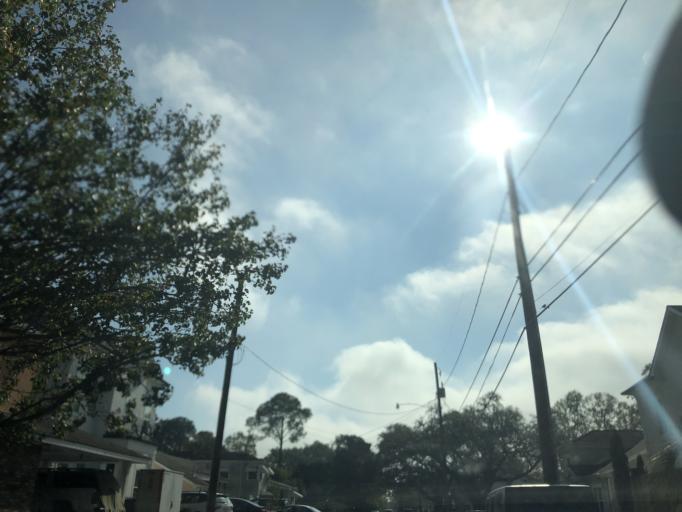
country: US
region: Louisiana
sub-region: Jefferson Parish
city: Metairie
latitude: 29.9840
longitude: -90.1520
